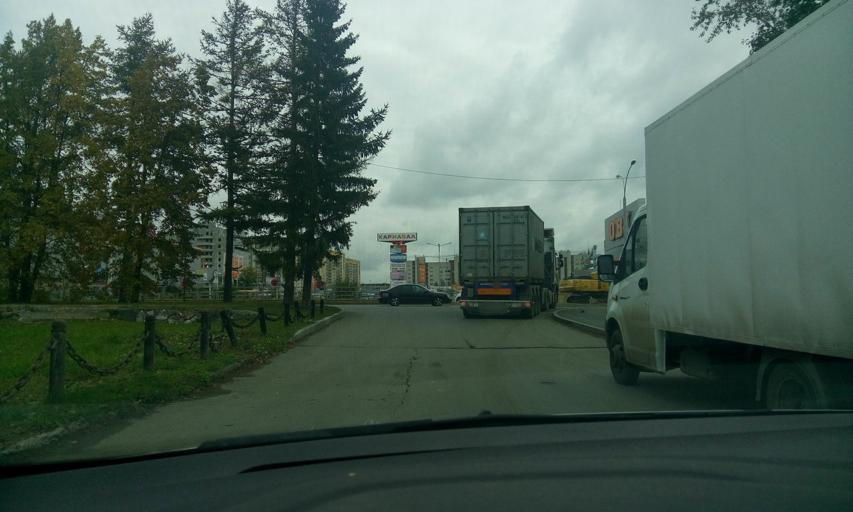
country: RU
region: Sverdlovsk
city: Yekaterinburg
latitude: 56.8512
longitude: 60.5488
